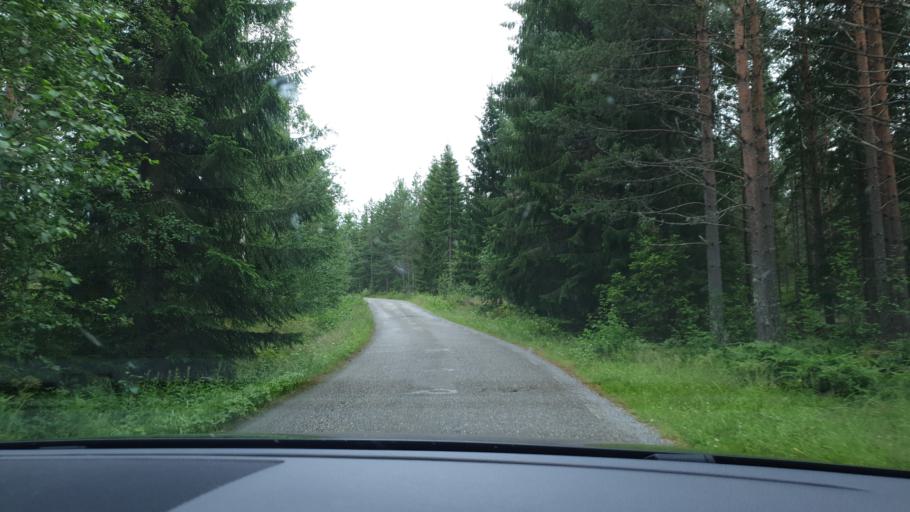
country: SE
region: Gaevleborg
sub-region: Hudiksvalls Kommun
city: Iggesund
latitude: 61.5351
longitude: 17.0104
